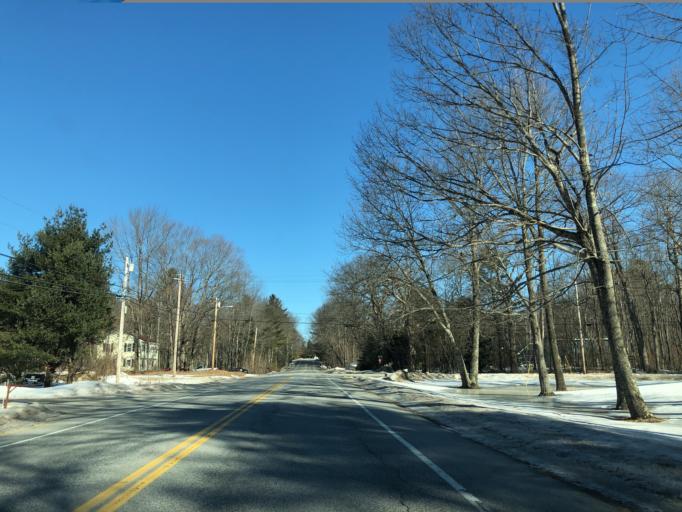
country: US
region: Maine
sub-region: Cumberland County
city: South Windham
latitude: 43.7661
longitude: -70.4218
